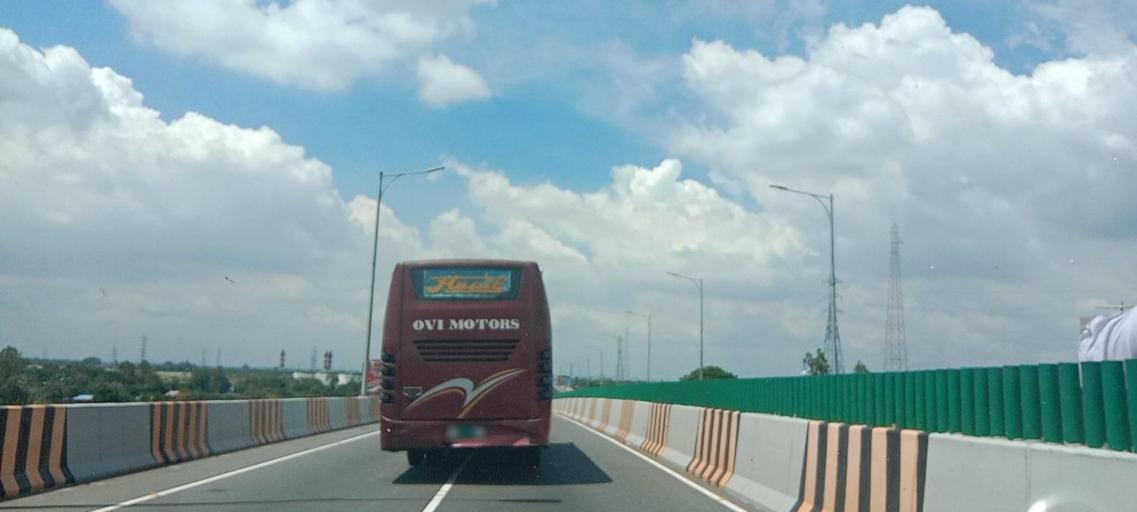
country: BD
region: Dhaka
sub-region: Dhaka
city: Dhaka
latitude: 23.6374
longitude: 90.3463
